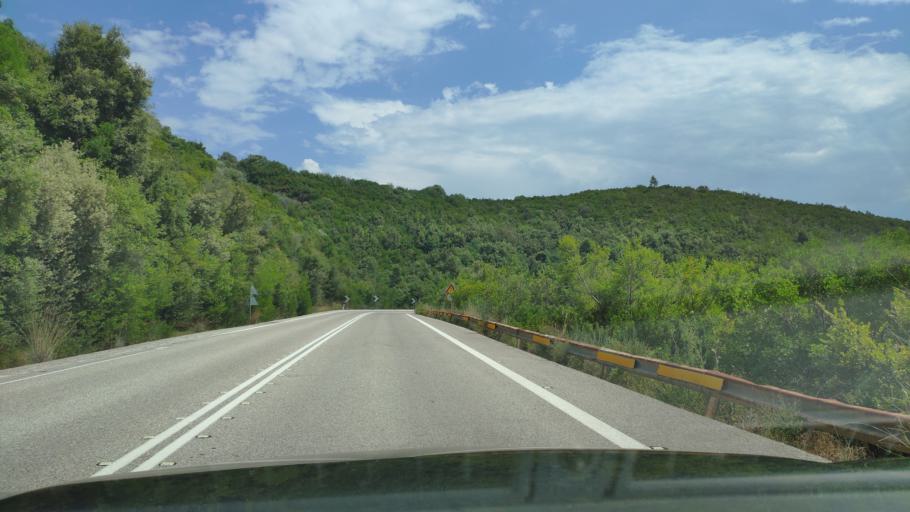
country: GR
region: West Greece
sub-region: Nomos Aitolias kai Akarnanias
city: Menidi
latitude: 39.0371
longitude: 21.1196
